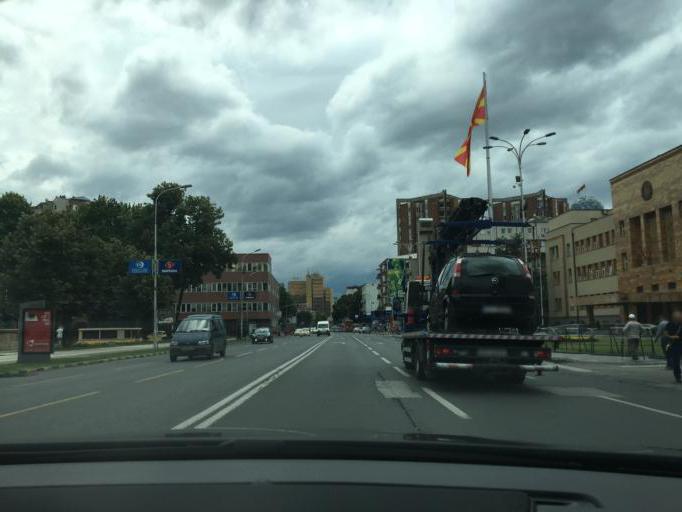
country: MK
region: Karpos
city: Skopje
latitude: 41.9937
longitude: 21.4328
